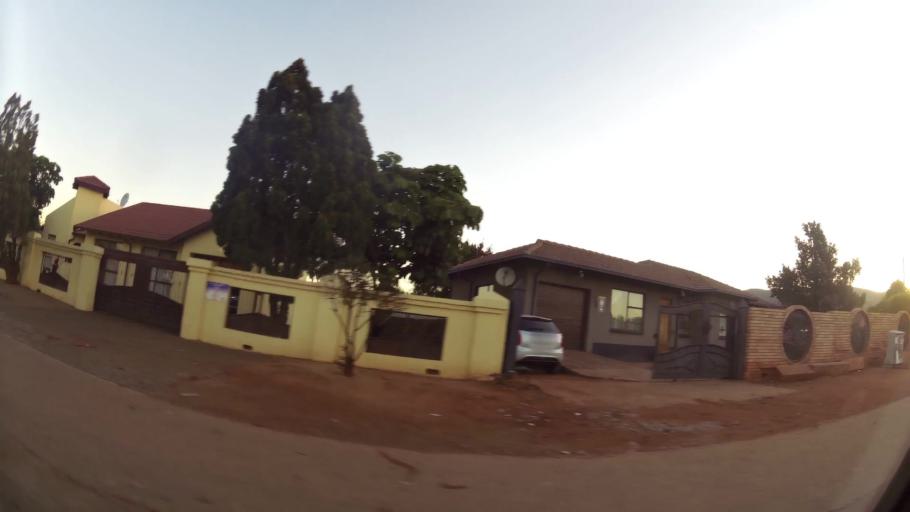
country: ZA
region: North-West
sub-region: Bojanala Platinum District Municipality
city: Rustenburg
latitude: -25.6560
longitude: 27.2111
